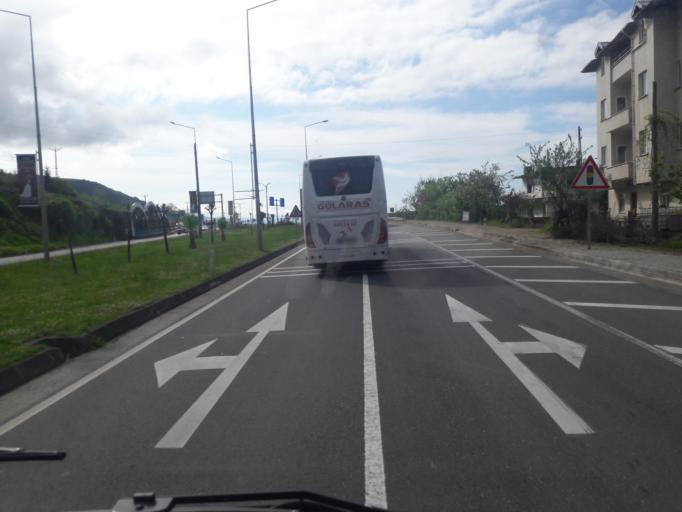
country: TR
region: Ordu
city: Gulyali
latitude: 40.9640
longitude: 38.0759
